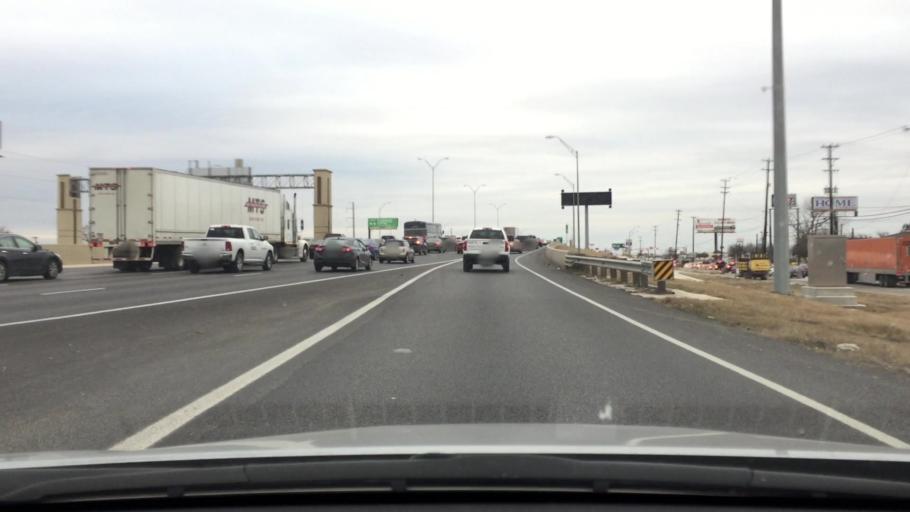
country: US
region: Texas
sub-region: Bexar County
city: Windcrest
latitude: 29.4939
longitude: -98.4009
